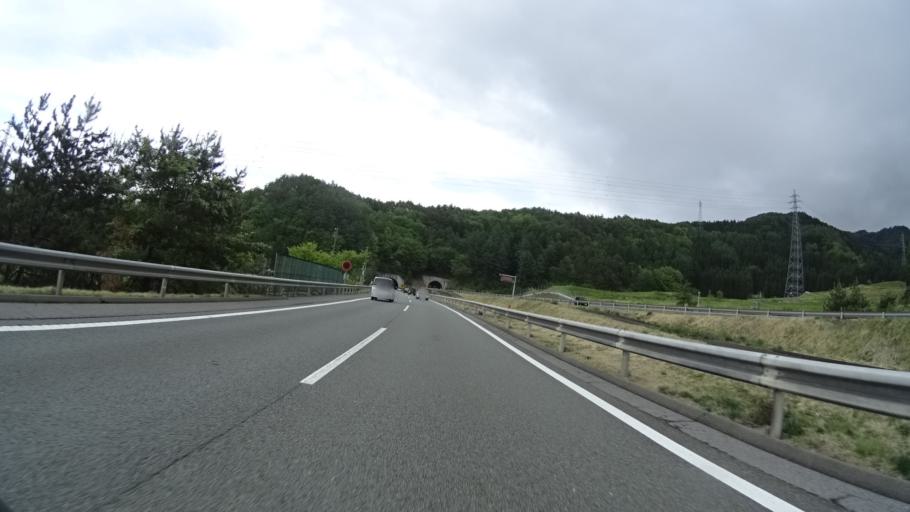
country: JP
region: Nagano
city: Nagano-shi
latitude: 36.5111
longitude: 138.0753
